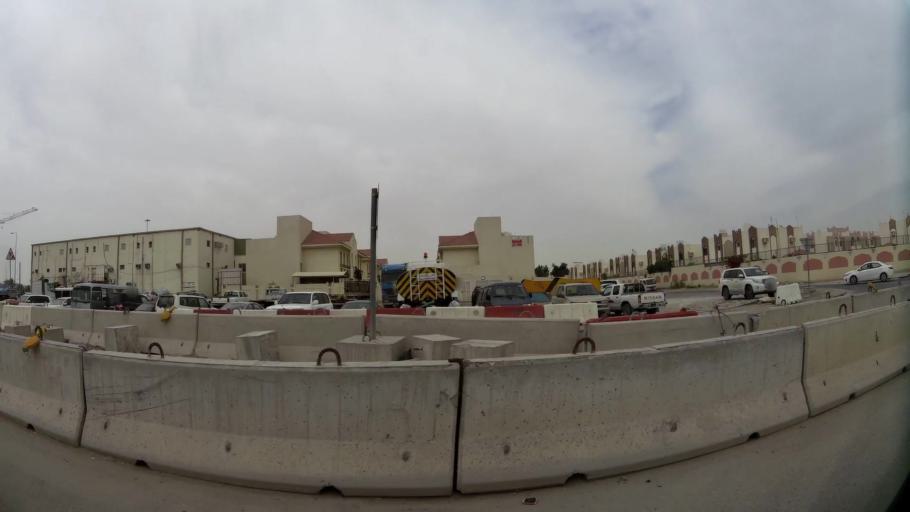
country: QA
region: Baladiyat ar Rayyan
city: Ar Rayyan
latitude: 25.2174
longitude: 51.4393
